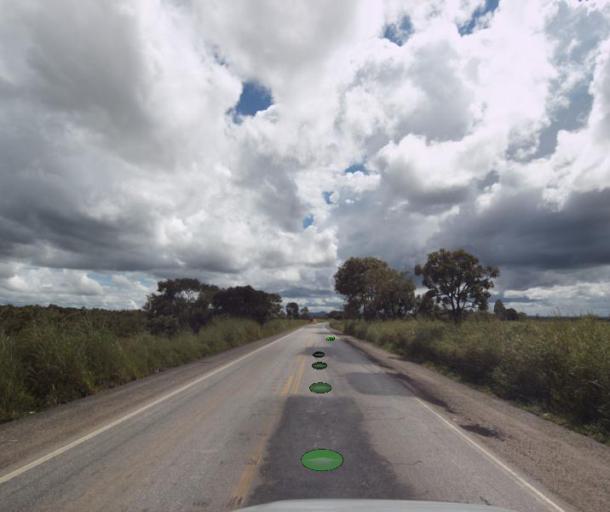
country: BR
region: Goias
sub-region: Uruacu
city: Uruacu
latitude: -14.2938
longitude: -49.1500
